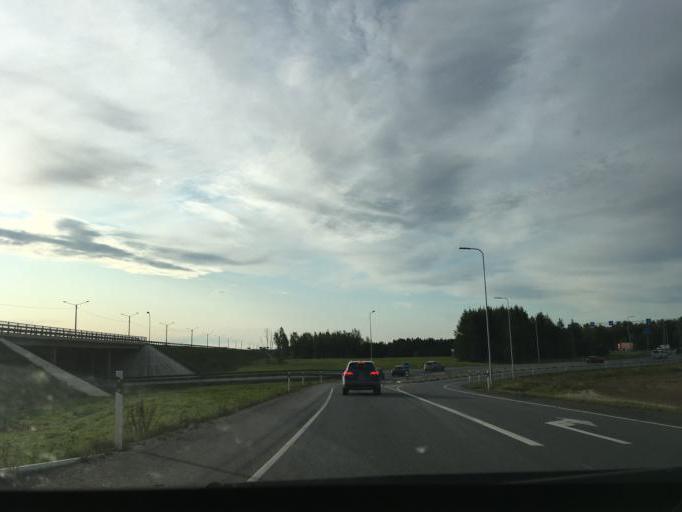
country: EE
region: Harju
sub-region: Rae vald
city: Jueri
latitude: 59.3549
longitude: 24.8788
